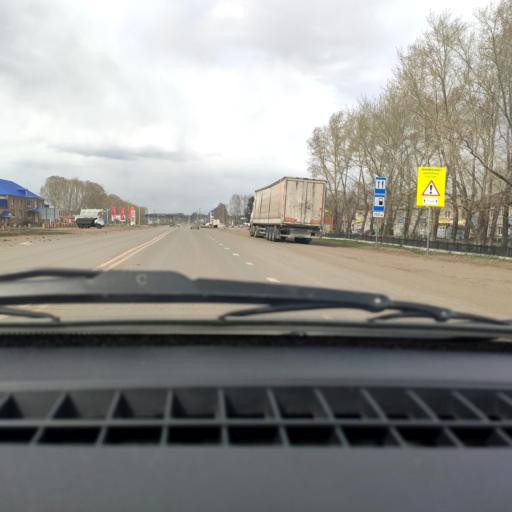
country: RU
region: Bashkortostan
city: Kushnarenkovo
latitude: 55.0992
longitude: 55.3350
